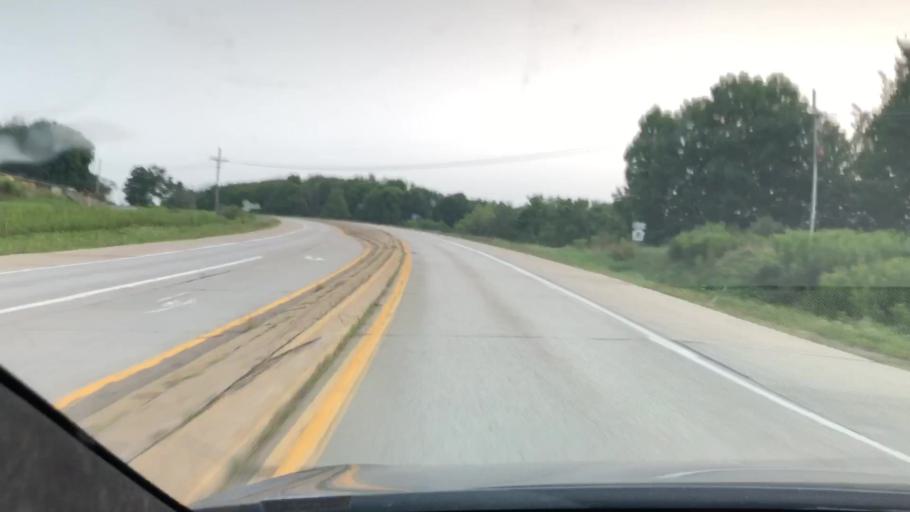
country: US
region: Pennsylvania
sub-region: Mercer County
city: Grove City
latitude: 41.2160
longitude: -79.9713
